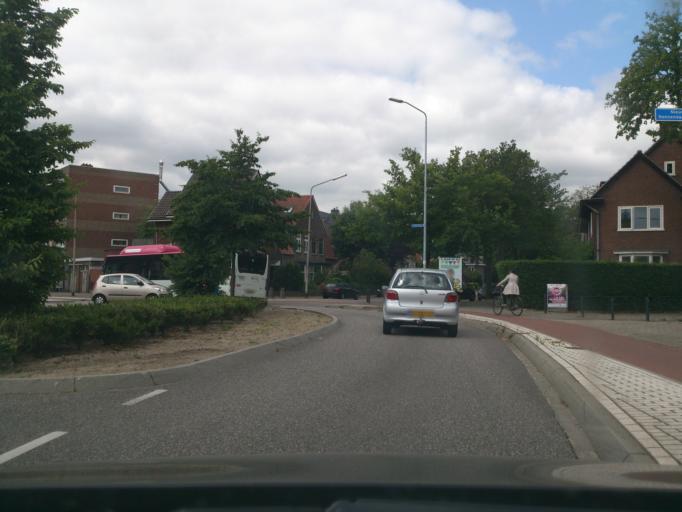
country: NL
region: Gelderland
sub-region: Gemeente Nijmegen
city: Nijmegen
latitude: 51.8422
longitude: 5.8410
